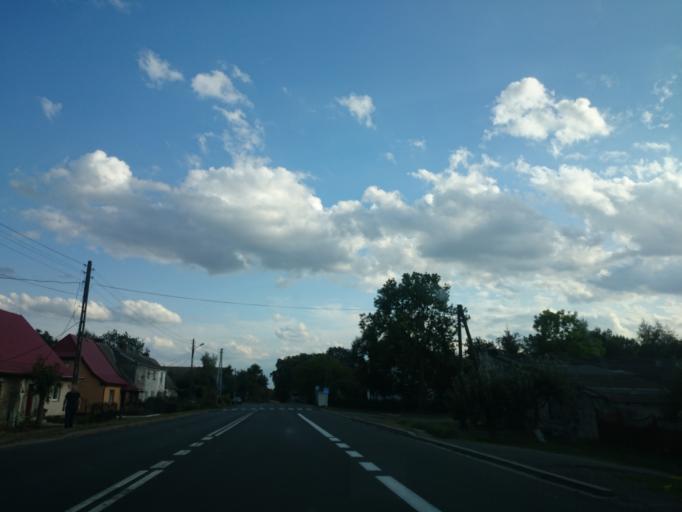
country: PL
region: West Pomeranian Voivodeship
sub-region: Powiat pyrzycki
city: Lipiany
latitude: 53.0587
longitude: 14.9101
